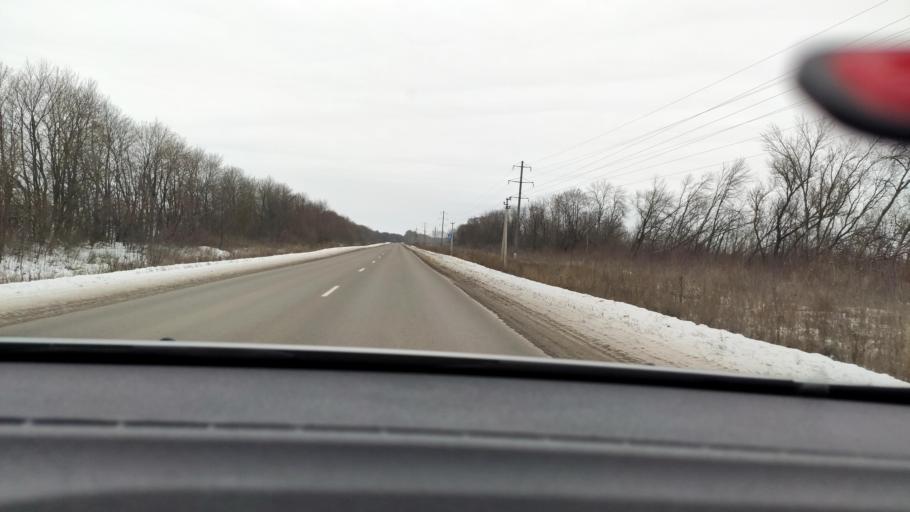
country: RU
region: Voronezj
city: Latnaya
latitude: 51.7605
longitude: 38.9149
